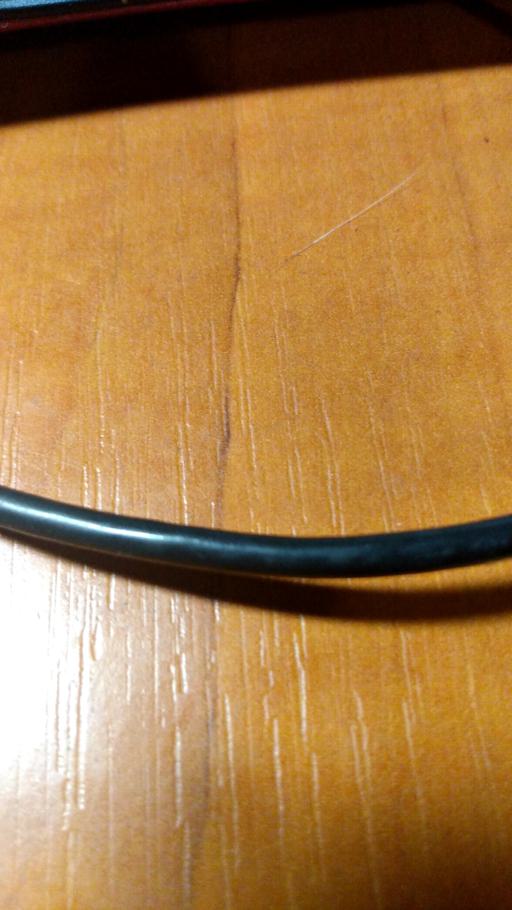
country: RU
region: Tverskaya
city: Toropets
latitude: 56.5032
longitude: 31.1471
